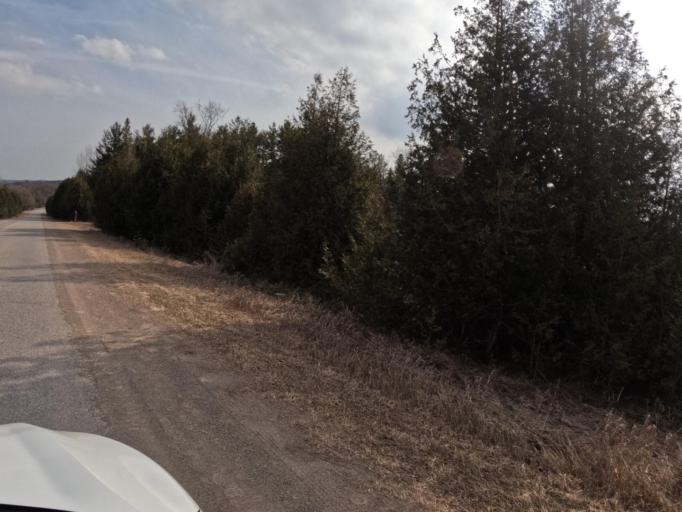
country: CA
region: Ontario
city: Orangeville
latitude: 43.9053
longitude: -80.2860
